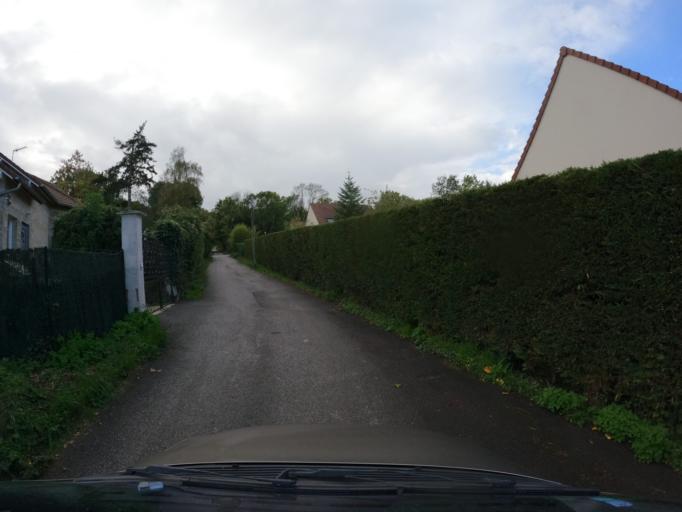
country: FR
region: Ile-de-France
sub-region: Departement de Seine-et-Marne
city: Saint-Germain-sur-Morin
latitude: 48.8771
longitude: 2.8541
